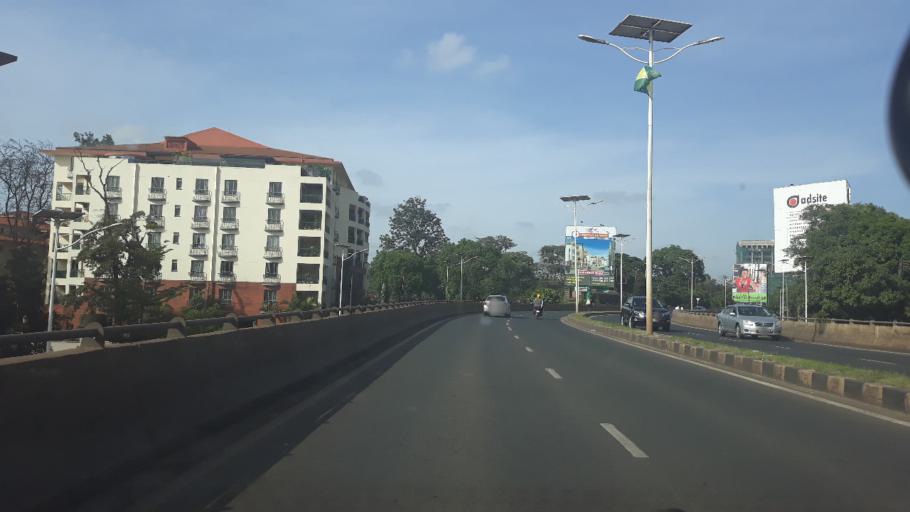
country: KE
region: Nairobi Area
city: Nairobi
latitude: -1.2716
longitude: 36.8146
